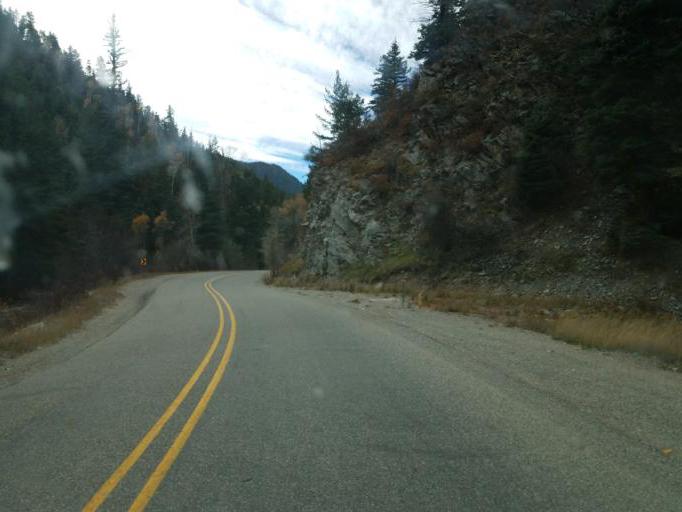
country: US
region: New Mexico
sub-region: Taos County
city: Arroyo Seco
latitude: 36.5669
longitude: -105.5233
